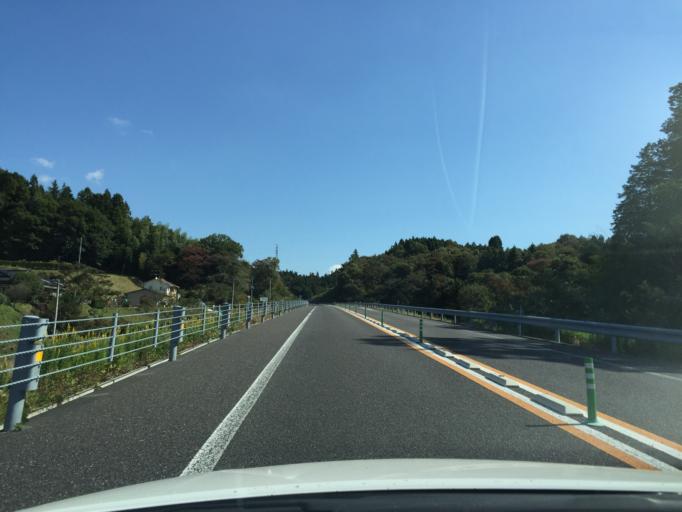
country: JP
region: Fukushima
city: Ishikawa
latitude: 37.2006
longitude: 140.4589
